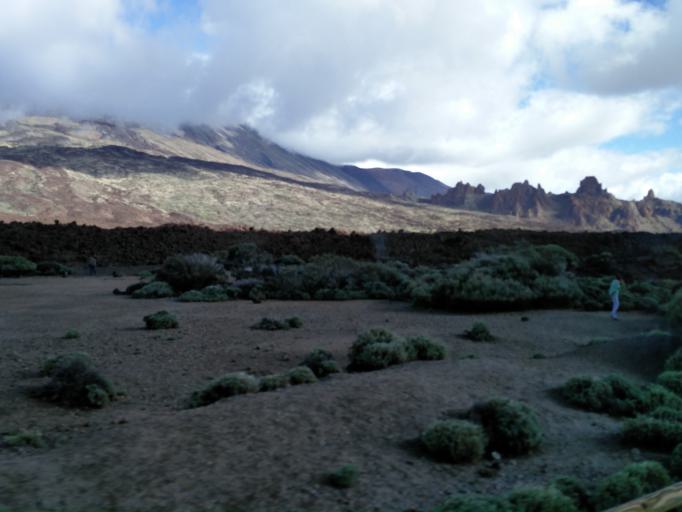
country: ES
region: Canary Islands
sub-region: Provincia de Santa Cruz de Tenerife
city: Vilaflor
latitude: 28.2108
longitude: -16.6562
